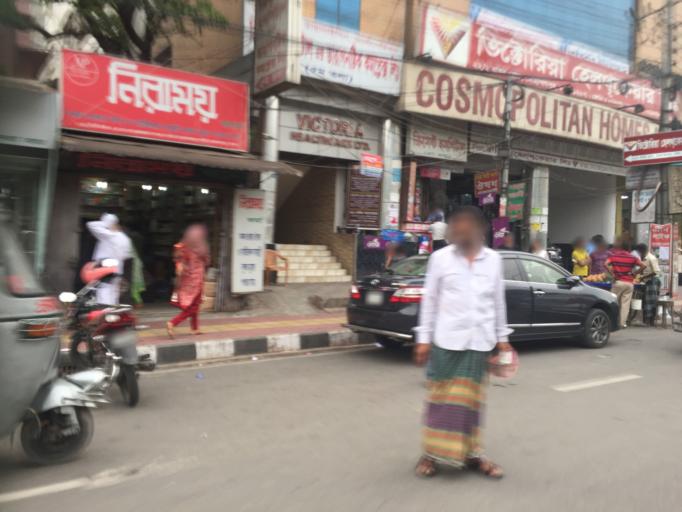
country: BD
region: Dhaka
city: Azimpur
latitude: 23.7708
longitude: 90.3681
